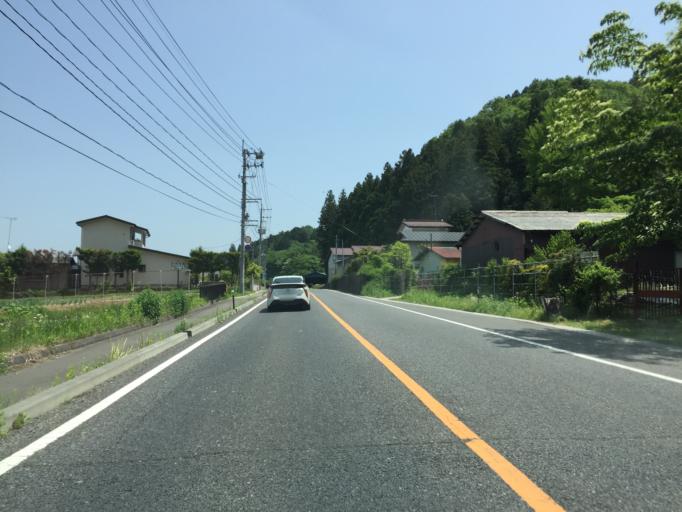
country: JP
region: Fukushima
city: Ishikawa
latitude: 37.1175
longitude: 140.3157
